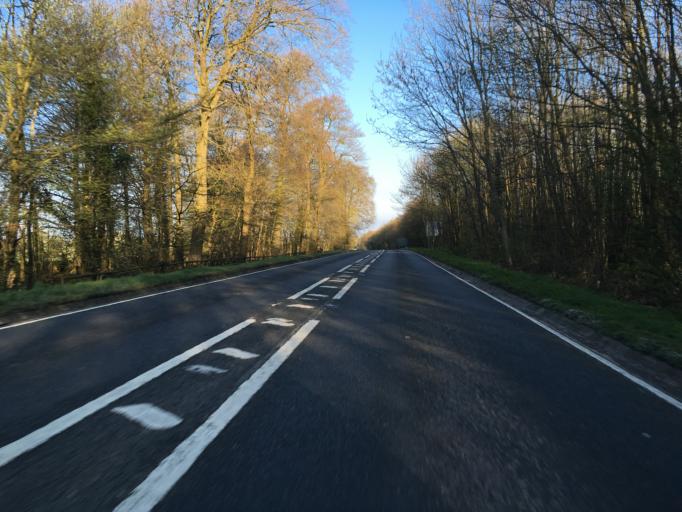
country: GB
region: England
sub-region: Gloucestershire
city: Bourton on the Water
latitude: 51.8230
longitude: -1.7778
